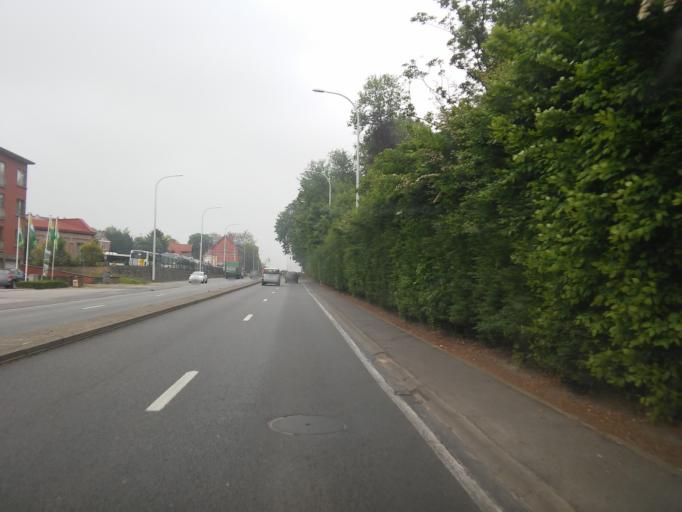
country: BE
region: Flanders
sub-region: Provincie Vlaams-Brabant
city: Dilbeek
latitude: 50.8430
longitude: 4.2529
